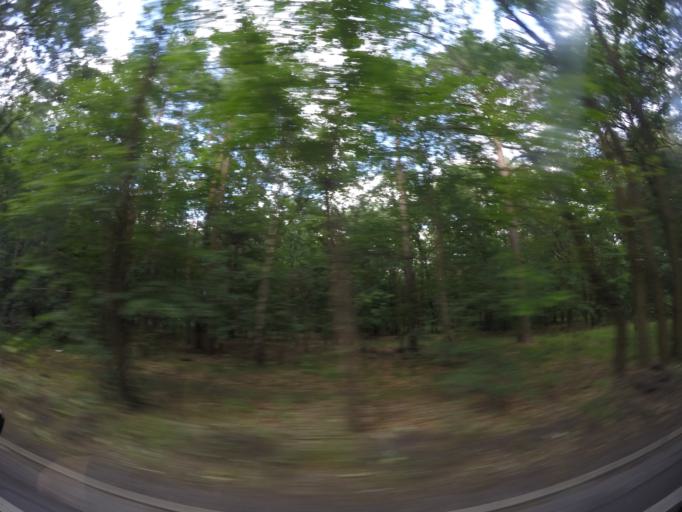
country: DE
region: Berlin
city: Kopenick Bezirk
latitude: 52.4630
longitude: 13.5580
